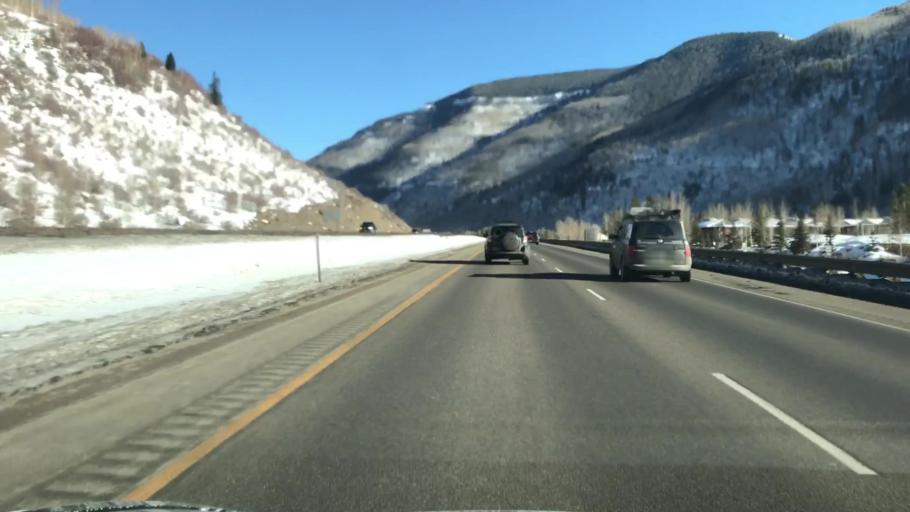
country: US
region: Colorado
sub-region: Eagle County
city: Vail
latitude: 39.6425
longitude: -106.3709
